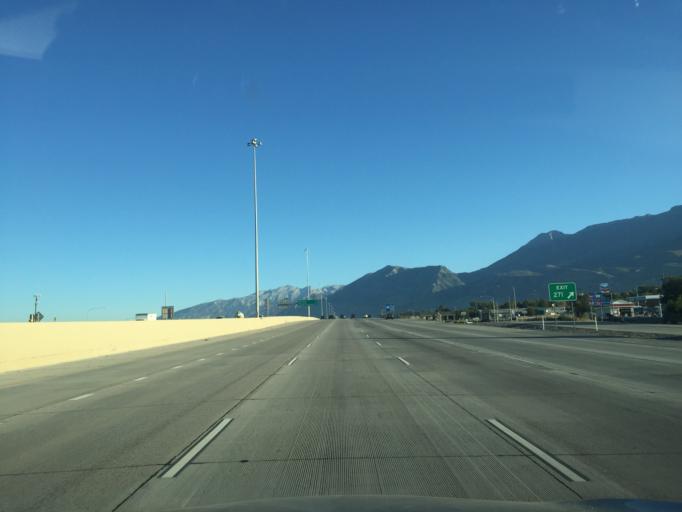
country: US
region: Utah
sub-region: Utah County
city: Orem
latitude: 40.2944
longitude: -111.7255
